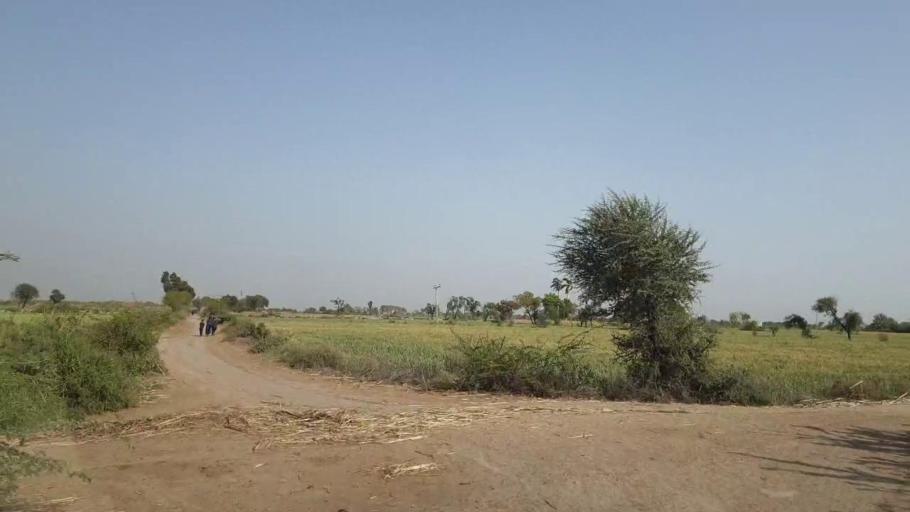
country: PK
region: Sindh
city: Tando Ghulam Ali
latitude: 25.0733
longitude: 68.8608
